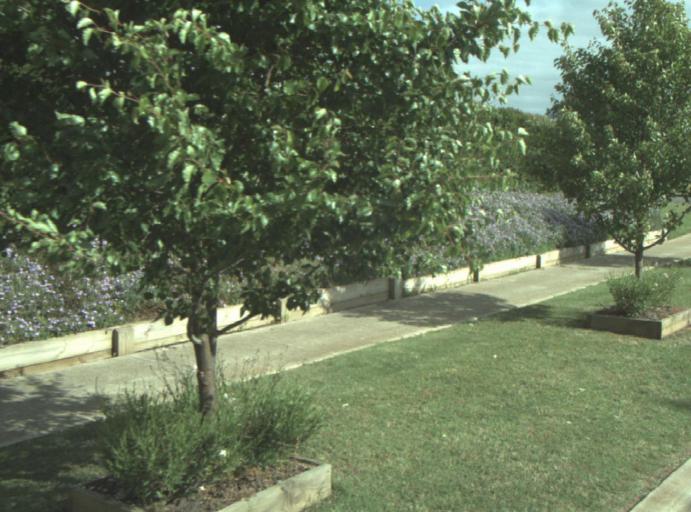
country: AU
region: Victoria
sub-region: Greater Geelong
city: Wandana Heights
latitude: -38.2100
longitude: 144.2991
